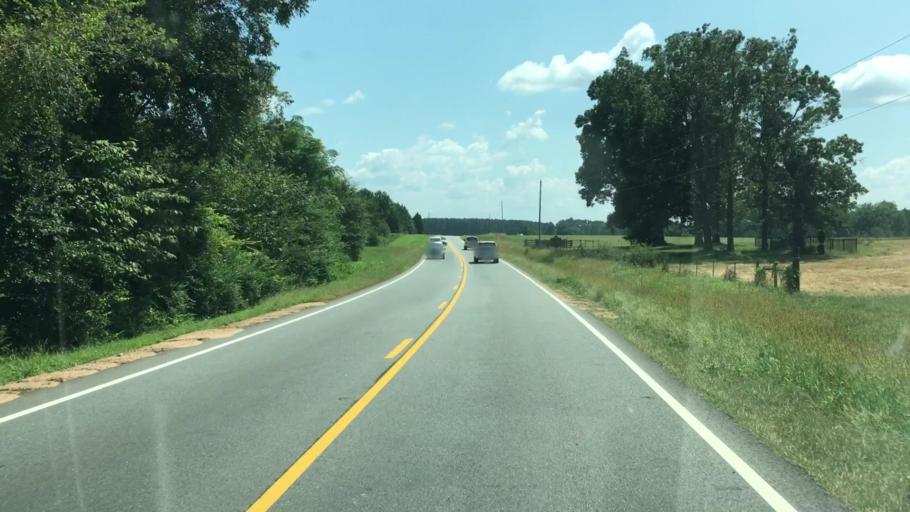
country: US
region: Georgia
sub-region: Oconee County
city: Watkinsville
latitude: 33.8013
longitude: -83.4266
